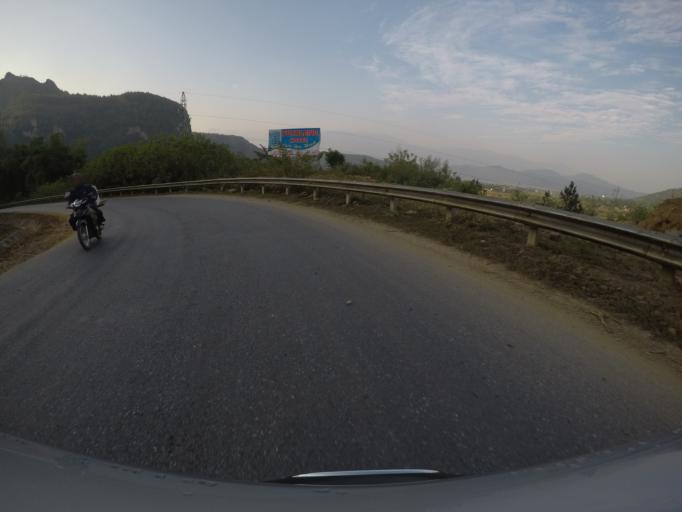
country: VN
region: Lai Chau
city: Tam Duong
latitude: 22.3220
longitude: 103.6571
